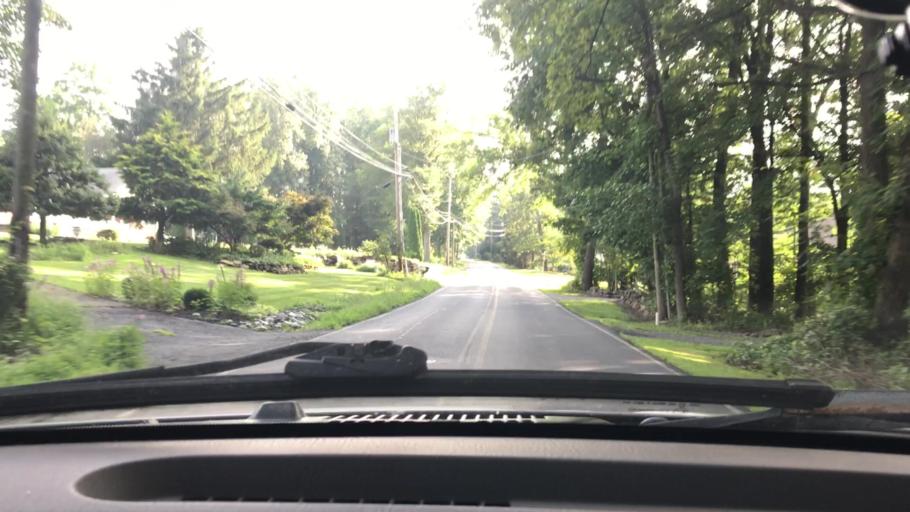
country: US
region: Pennsylvania
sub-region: Dauphin County
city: Hershey
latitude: 40.2272
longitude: -76.6272
